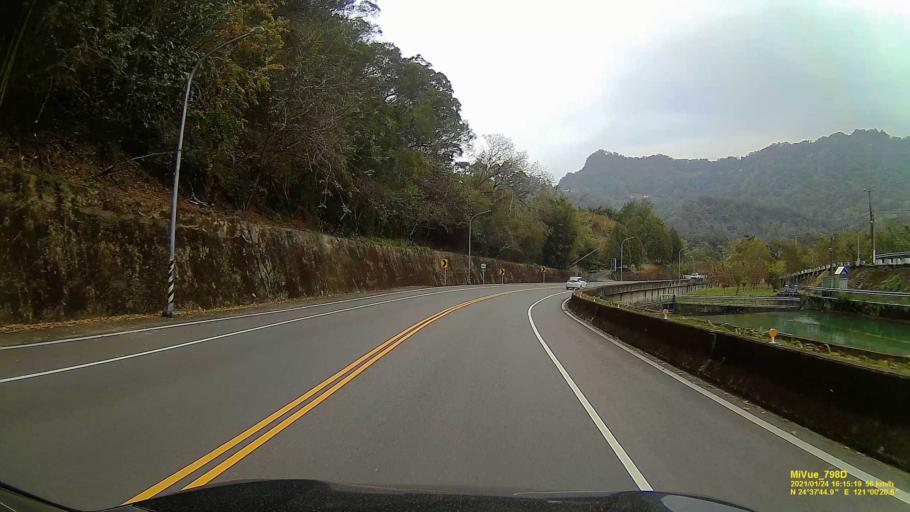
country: TW
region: Taiwan
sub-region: Hsinchu
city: Hsinchu
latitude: 24.6295
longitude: 121.0058
